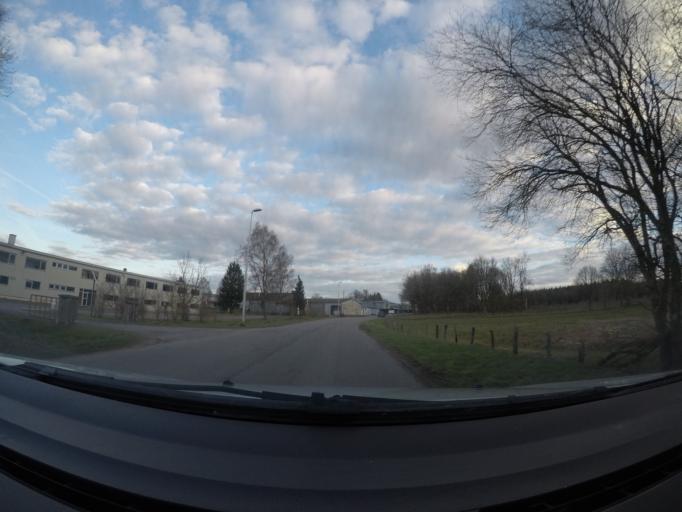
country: BE
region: Wallonia
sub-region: Province du Luxembourg
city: Etalle
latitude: 49.6674
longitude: 5.5701
